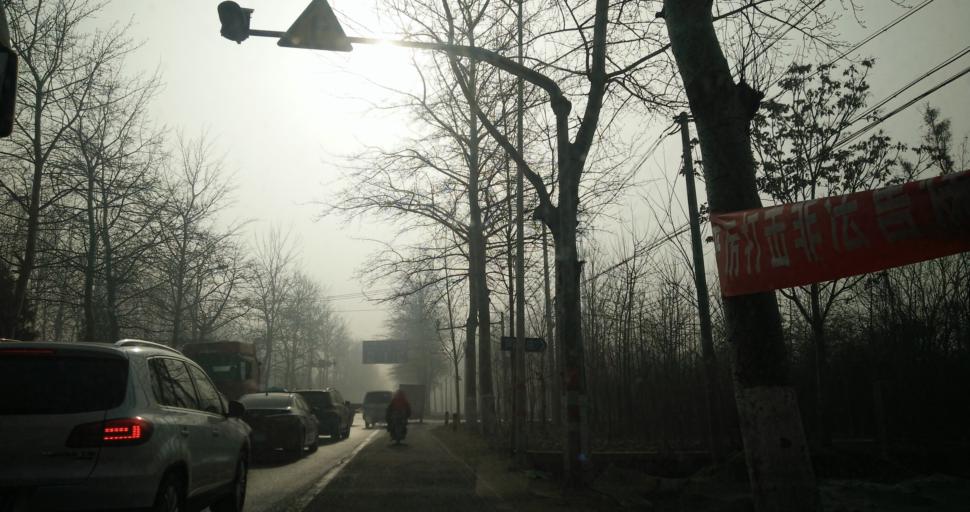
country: CN
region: Beijing
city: Yinghai
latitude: 39.7475
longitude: 116.4471
